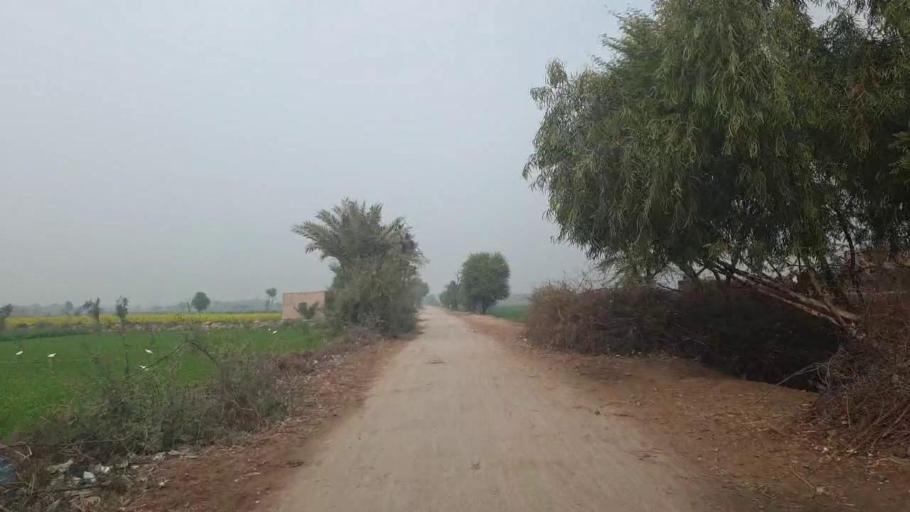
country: PK
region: Sindh
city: Tando Adam
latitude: 25.7570
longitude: 68.7025
